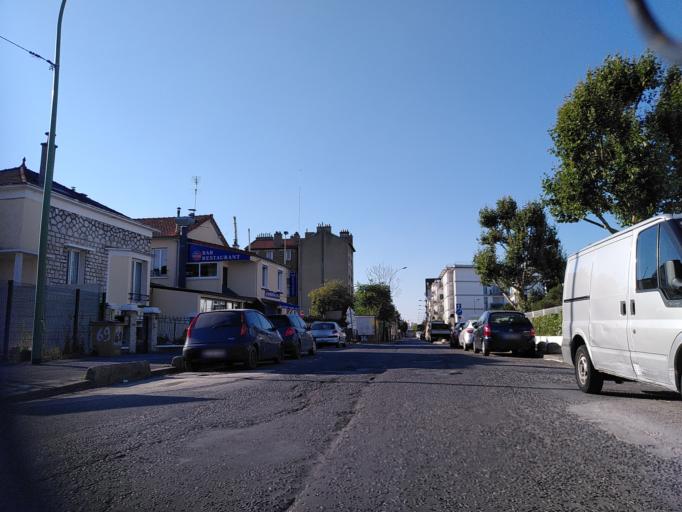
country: FR
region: Ile-de-France
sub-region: Departement du Val-de-Marne
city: Alfortville
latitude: 48.8005
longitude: 2.4107
